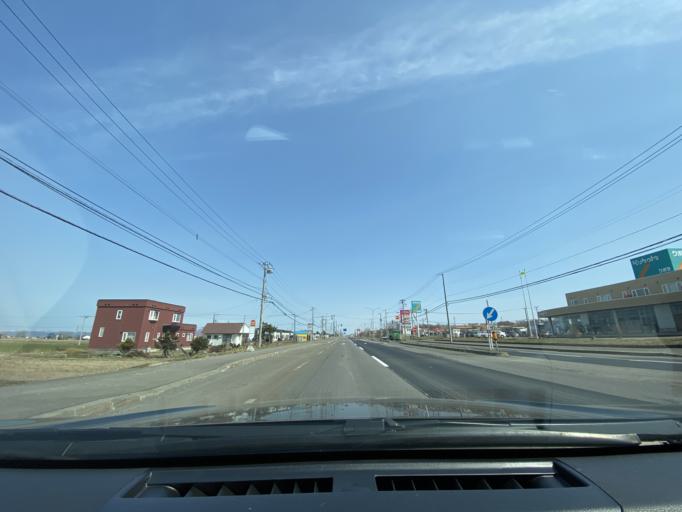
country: JP
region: Hokkaido
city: Iwamizawa
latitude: 43.2414
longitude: 141.8025
